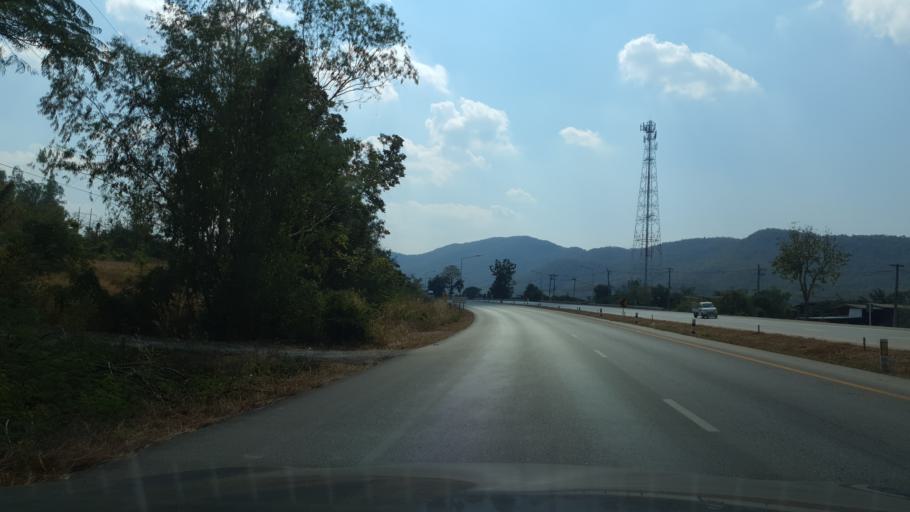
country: TH
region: Lampang
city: Mae Phrik
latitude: 17.3653
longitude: 99.1471
